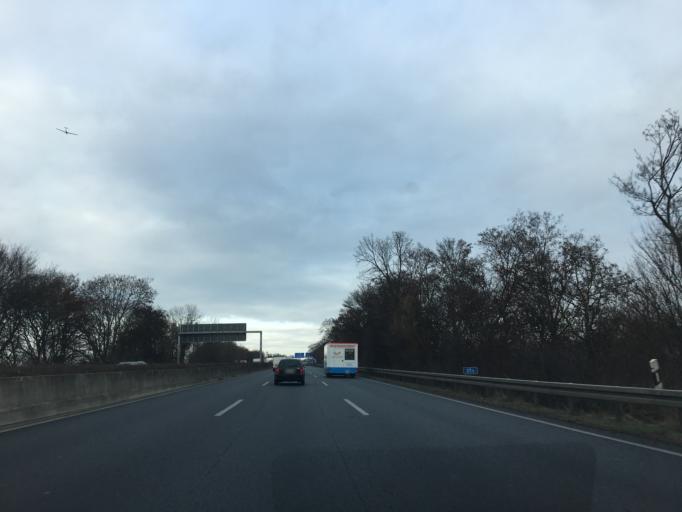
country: DE
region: North Rhine-Westphalia
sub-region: Regierungsbezirk Koln
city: Bonn
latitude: 50.7564
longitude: 7.1401
